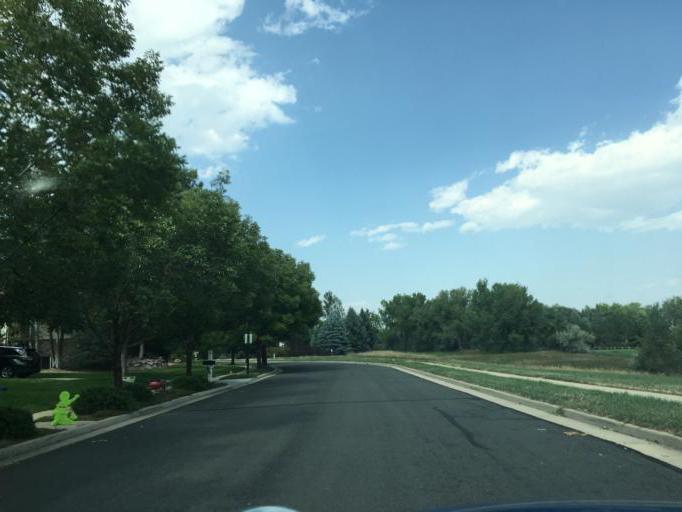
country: US
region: Colorado
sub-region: Boulder County
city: Lafayette
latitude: 40.0183
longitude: -105.1185
